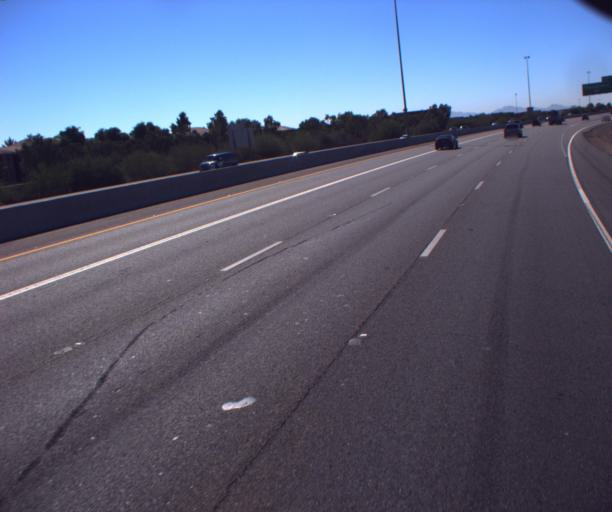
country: US
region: Arizona
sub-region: Maricopa County
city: Peoria
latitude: 33.6161
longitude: -112.2398
